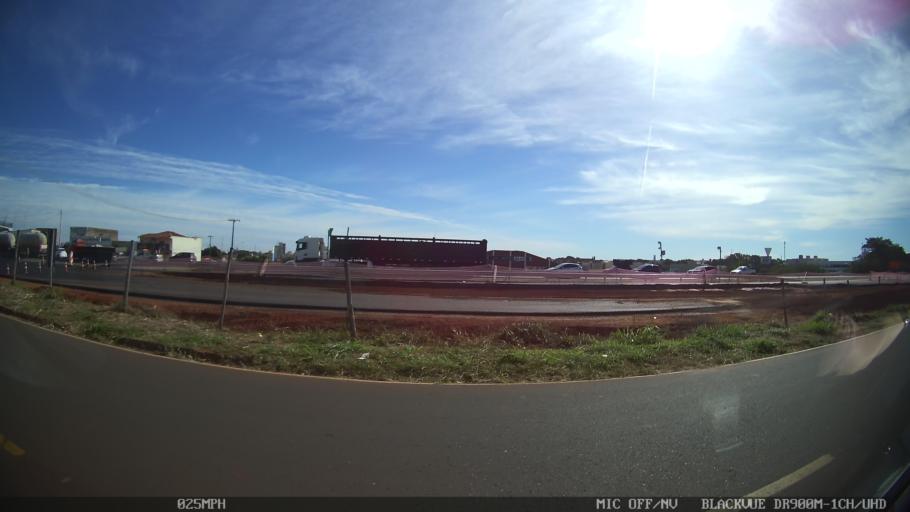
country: BR
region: Sao Paulo
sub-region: Sao Jose Do Rio Preto
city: Sao Jose do Rio Preto
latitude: -20.7973
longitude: -49.3548
